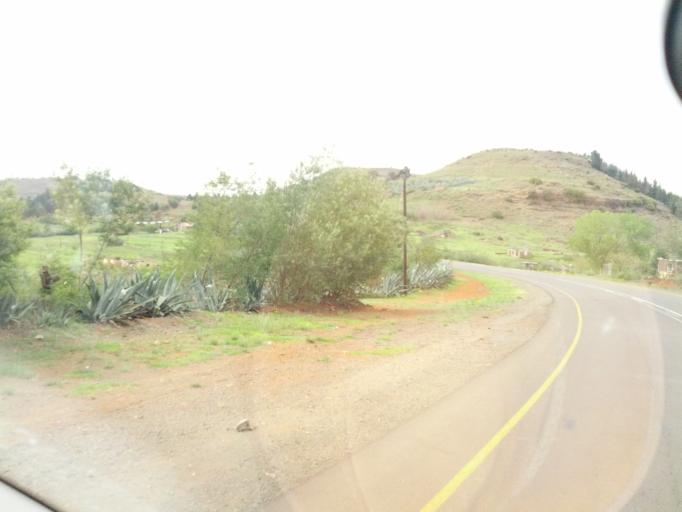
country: LS
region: Maseru
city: Nako
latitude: -29.4895
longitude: 27.7487
